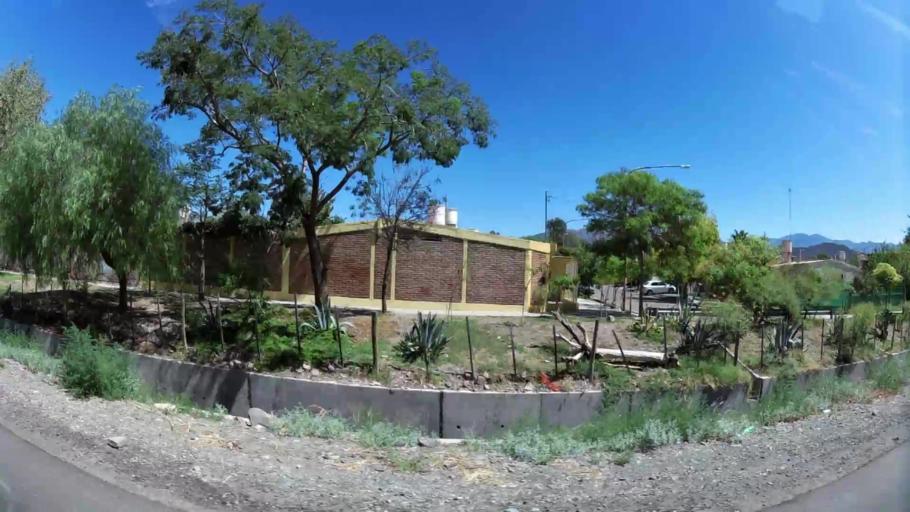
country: AR
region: Mendoza
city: Las Heras
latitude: -32.8451
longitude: -68.8614
